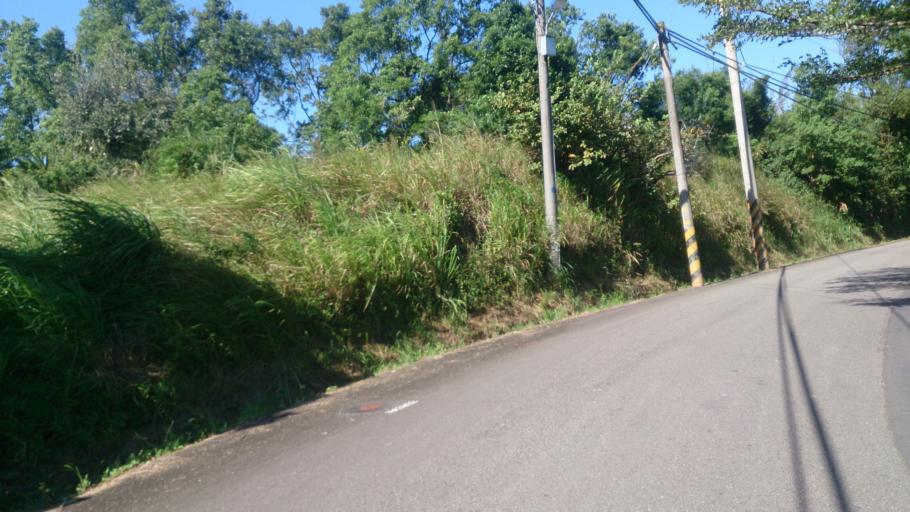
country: TW
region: Taiwan
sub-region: Hsinchu
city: Hsinchu
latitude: 24.7524
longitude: 120.9495
